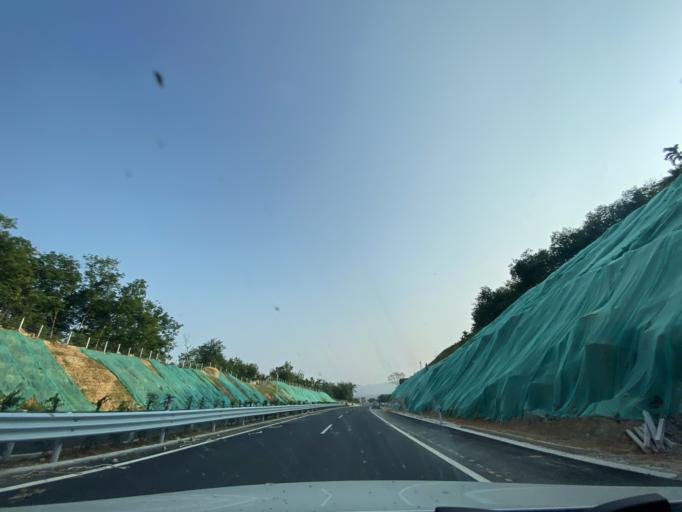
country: CN
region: Hainan
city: Xiangshui
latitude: 18.6475
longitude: 109.6295
